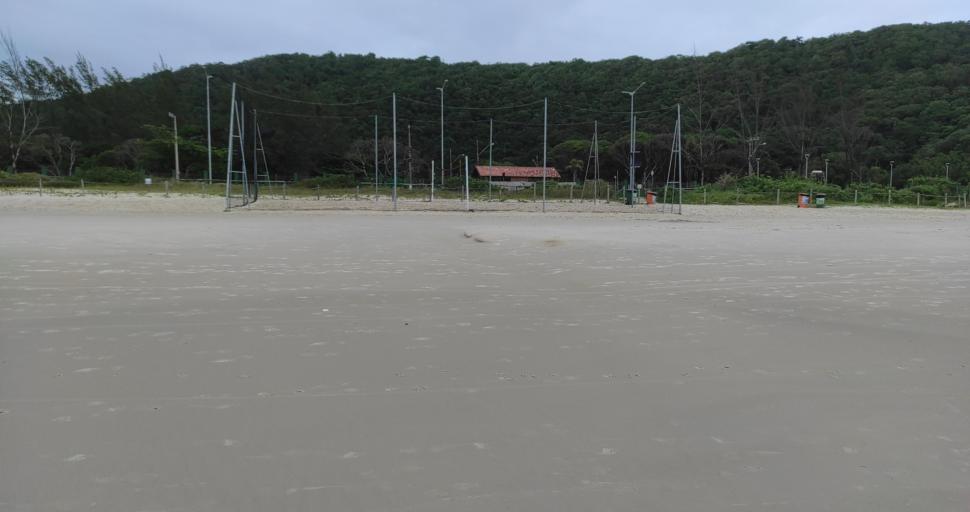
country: BR
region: Santa Catarina
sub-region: Porto Belo
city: Porto Belo
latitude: -27.1683
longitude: -48.4978
